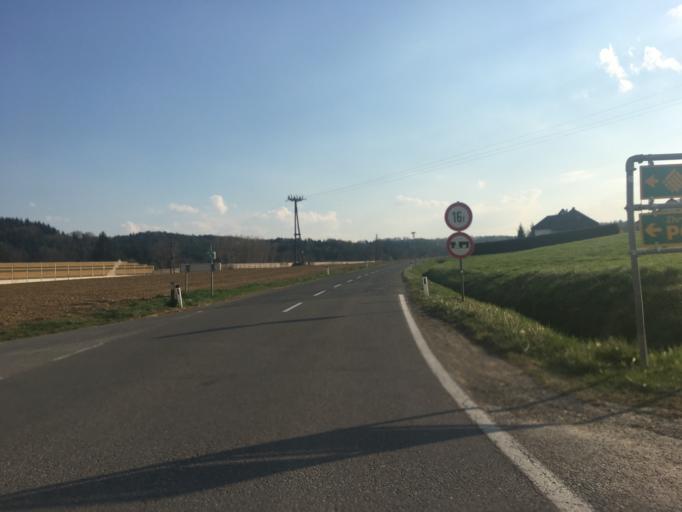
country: AT
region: Styria
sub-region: Politischer Bezirk Weiz
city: Ungerdorf
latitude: 47.0821
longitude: 15.6461
